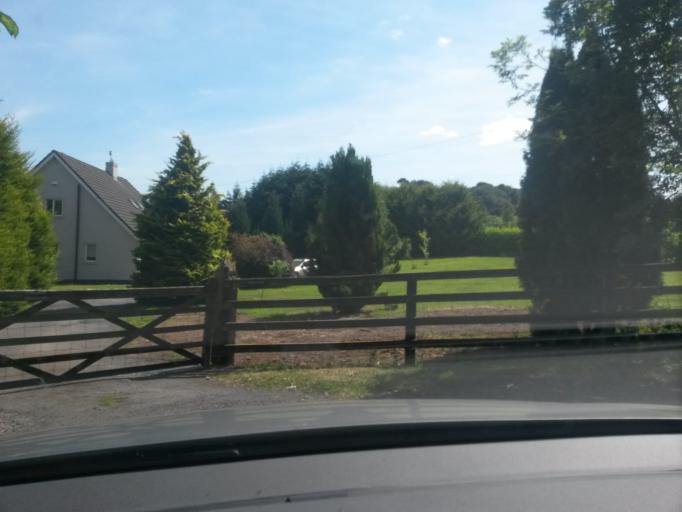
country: IE
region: Leinster
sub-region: Kildare
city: Eadestown
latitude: 53.2032
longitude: -6.5770
